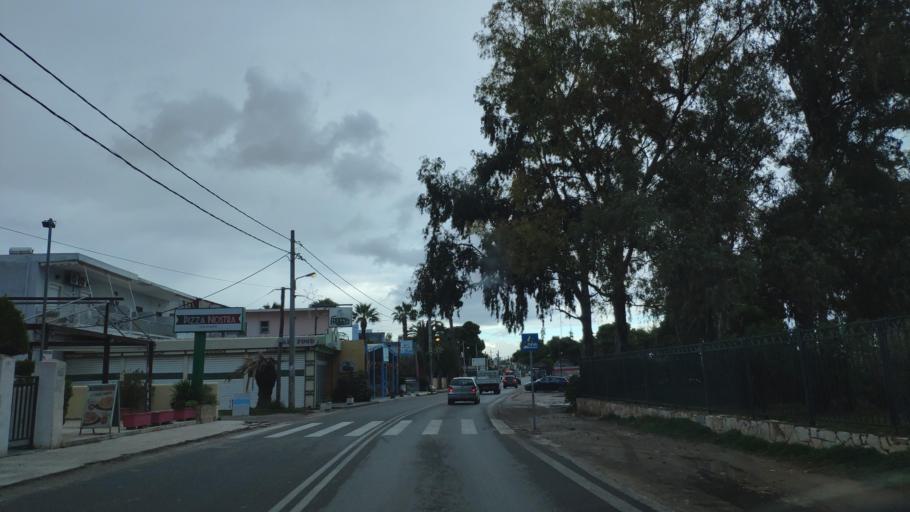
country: GR
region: Attica
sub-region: Nomarchia Anatolikis Attikis
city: Artemida
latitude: 37.9798
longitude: 24.0085
